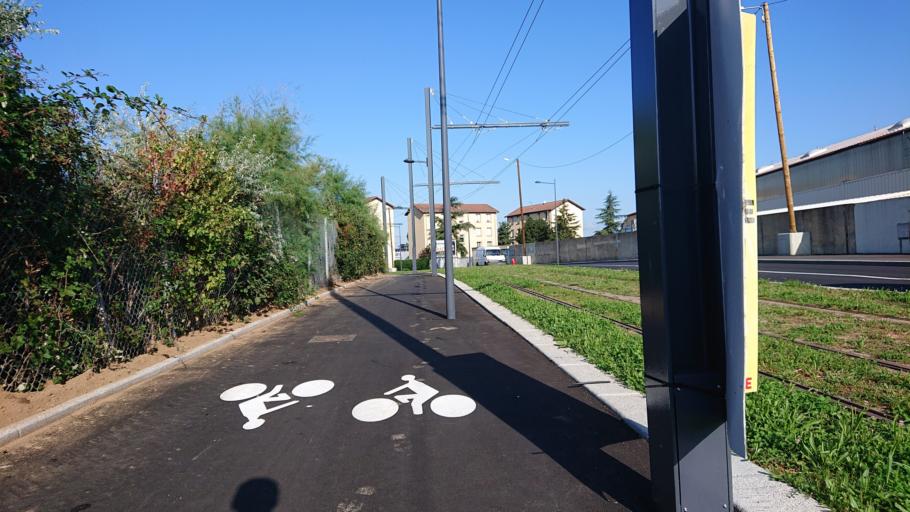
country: FR
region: Rhone-Alpes
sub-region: Departement de la Loire
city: Saint-Etienne
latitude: 45.4538
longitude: 4.3982
